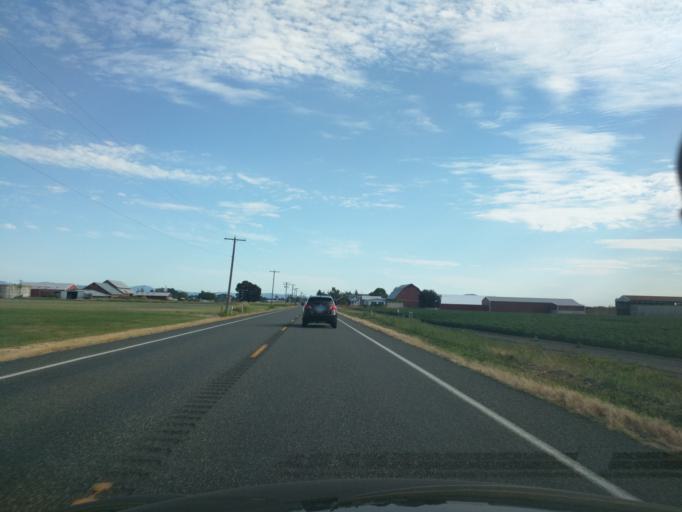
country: US
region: Washington
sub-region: Whatcom County
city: Lynden
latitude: 48.9723
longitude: -122.4853
